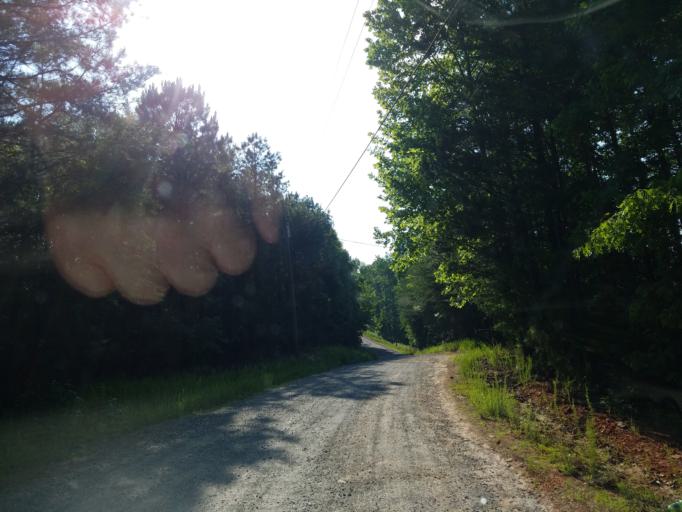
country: US
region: Georgia
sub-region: Pickens County
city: Nelson
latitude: 34.3712
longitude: -84.3367
